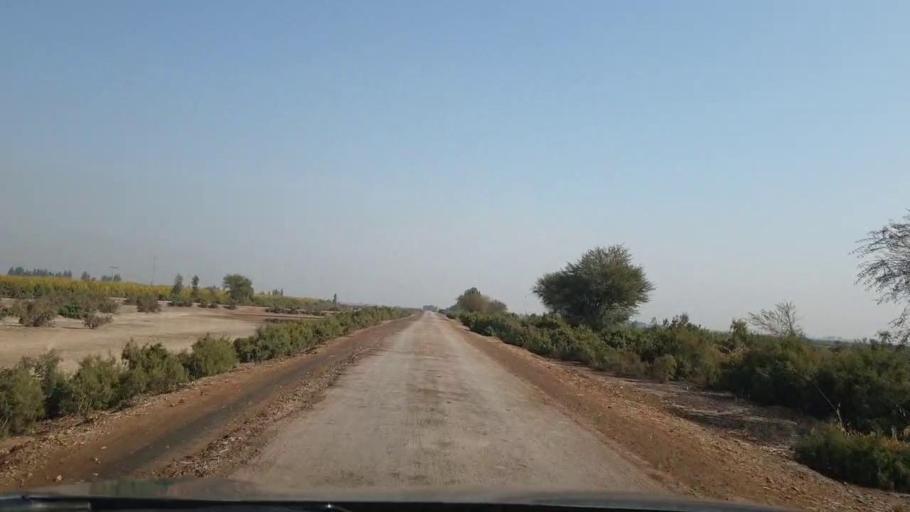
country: PK
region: Sindh
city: Berani
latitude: 25.6356
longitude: 68.8664
